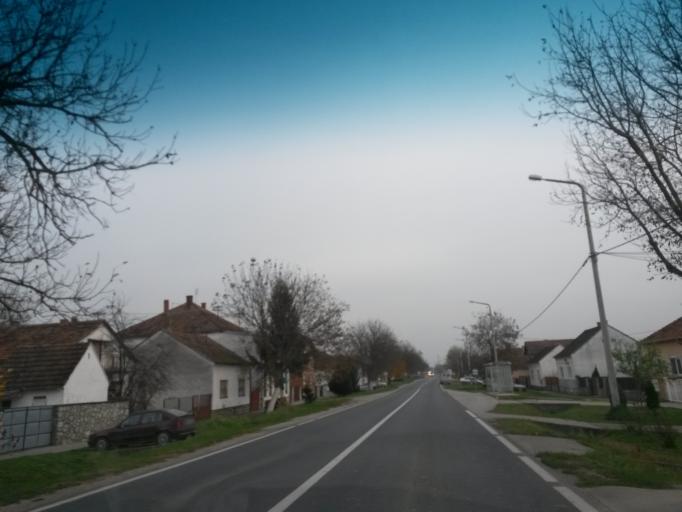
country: HR
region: Vukovarsko-Srijemska
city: Mirkovci
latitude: 45.2762
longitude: 18.8381
